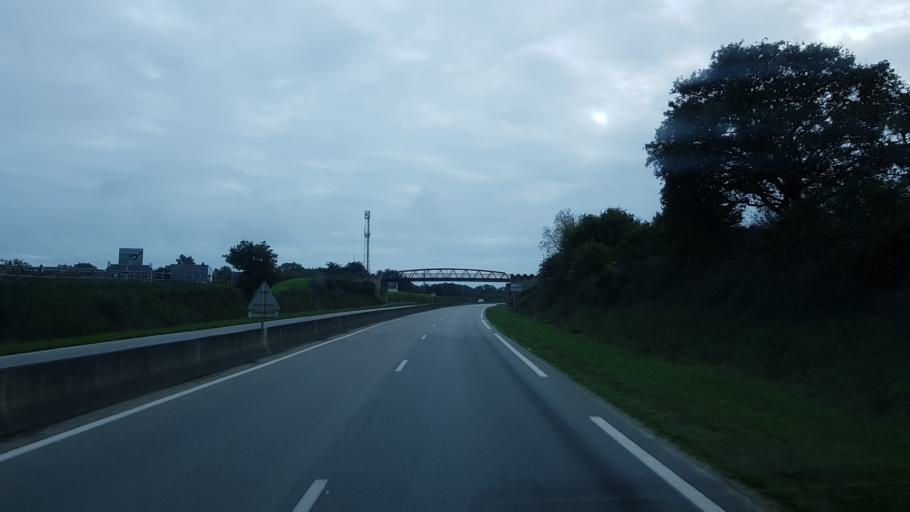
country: FR
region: Brittany
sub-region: Departement du Morbihan
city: Sarzeau
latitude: 47.5490
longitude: -2.7185
